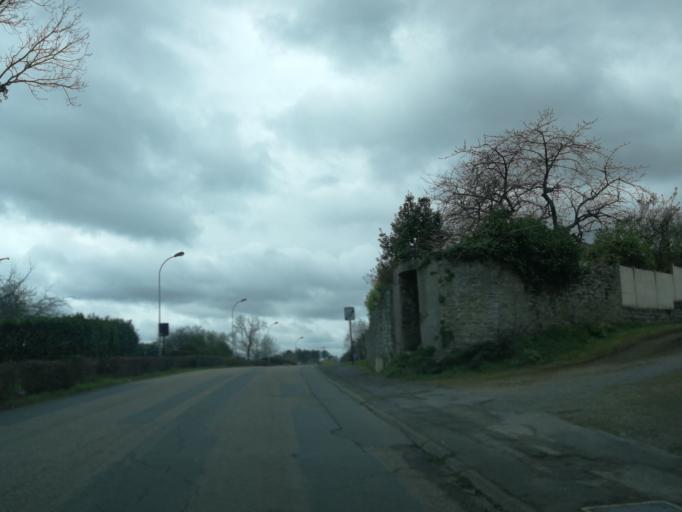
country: FR
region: Brittany
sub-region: Departement d'Ille-et-Vilaine
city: Guichen
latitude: 47.9647
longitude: -1.7989
